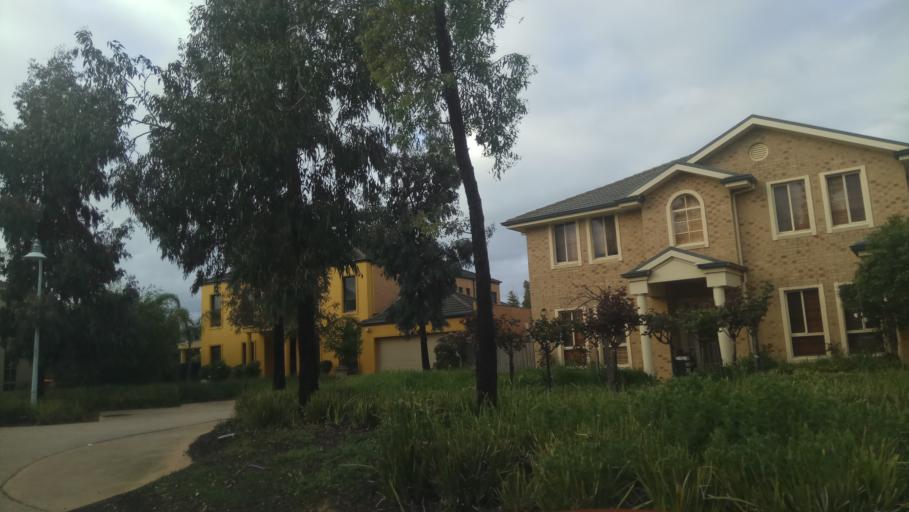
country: AU
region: Victoria
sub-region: Wyndham
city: Point Cook
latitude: -37.9002
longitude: 144.7597
